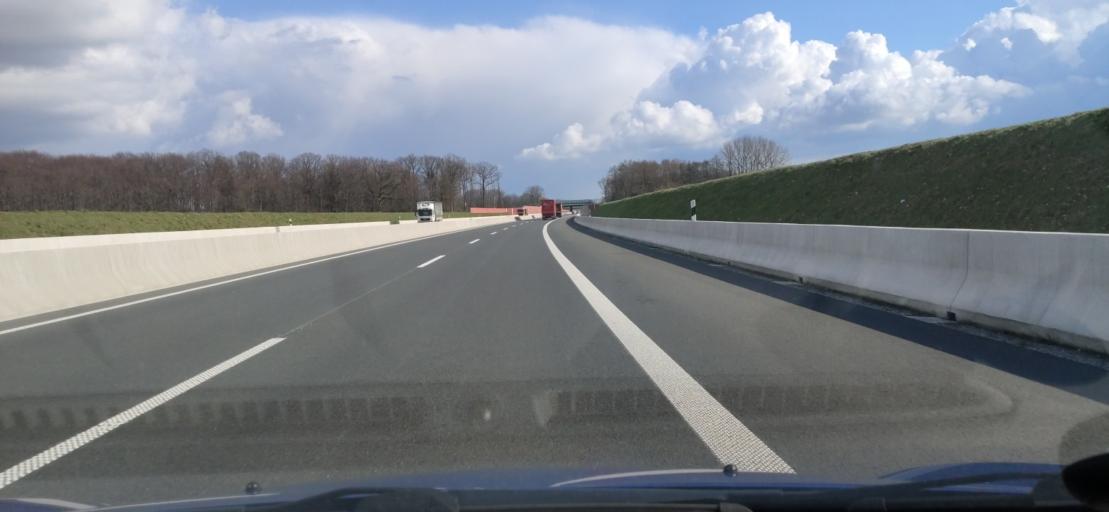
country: DE
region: North Rhine-Westphalia
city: Borgholzhausen
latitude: 52.0684
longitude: 8.2978
